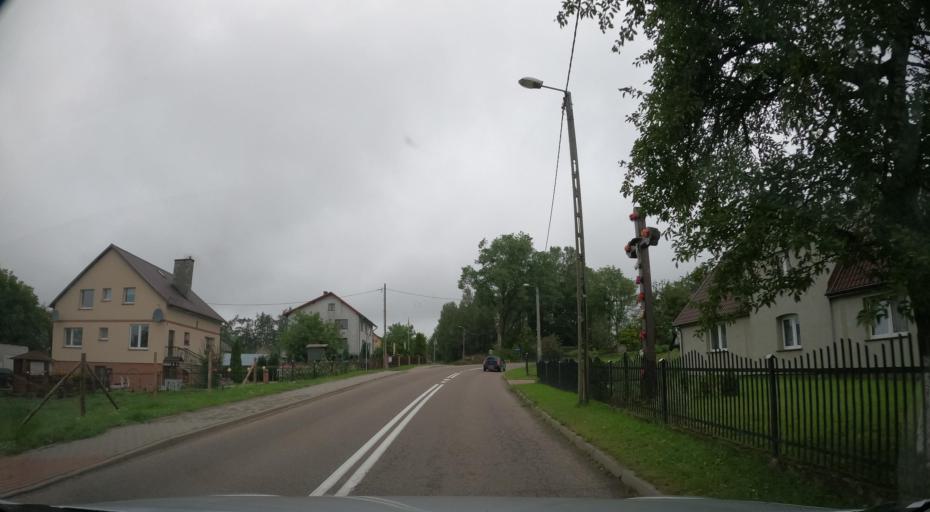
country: PL
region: Pomeranian Voivodeship
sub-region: Powiat wejherowski
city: Luzino
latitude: 54.4700
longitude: 18.0736
